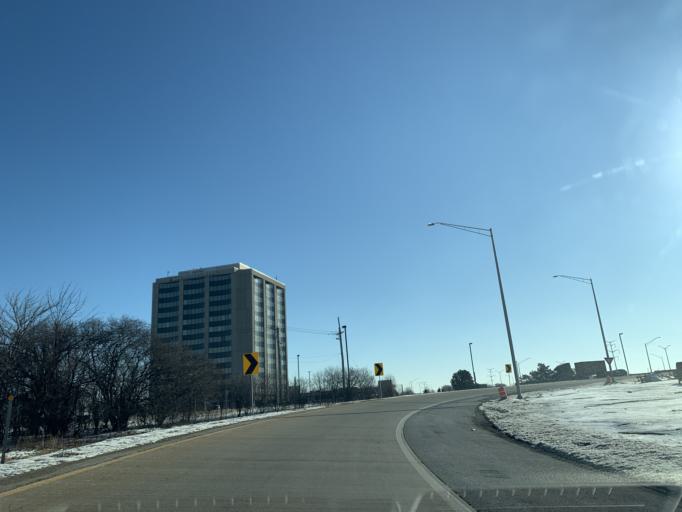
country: US
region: Illinois
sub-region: DuPage County
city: Oakbrook Terrace
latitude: 41.8459
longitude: -87.9589
